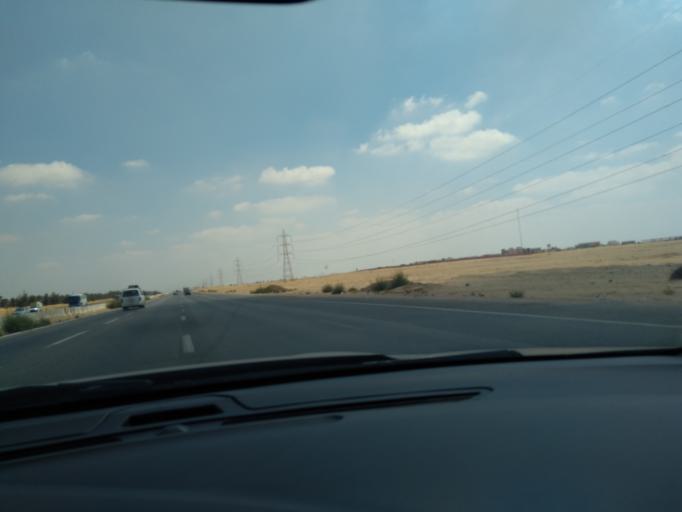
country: EG
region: Al Isma'iliyah
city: At Tall al Kabir
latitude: 30.3877
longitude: 31.9599
